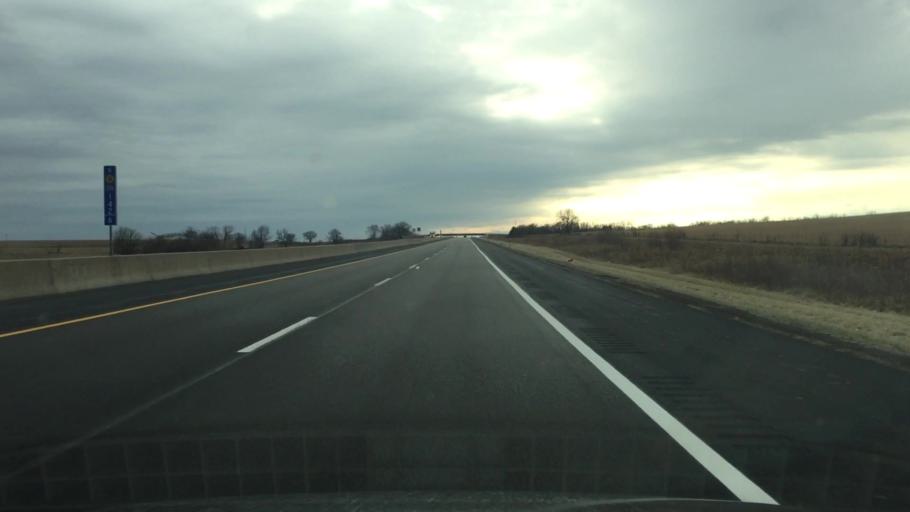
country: US
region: Kansas
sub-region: Lyon County
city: Emporia
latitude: 38.5985
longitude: -96.0714
